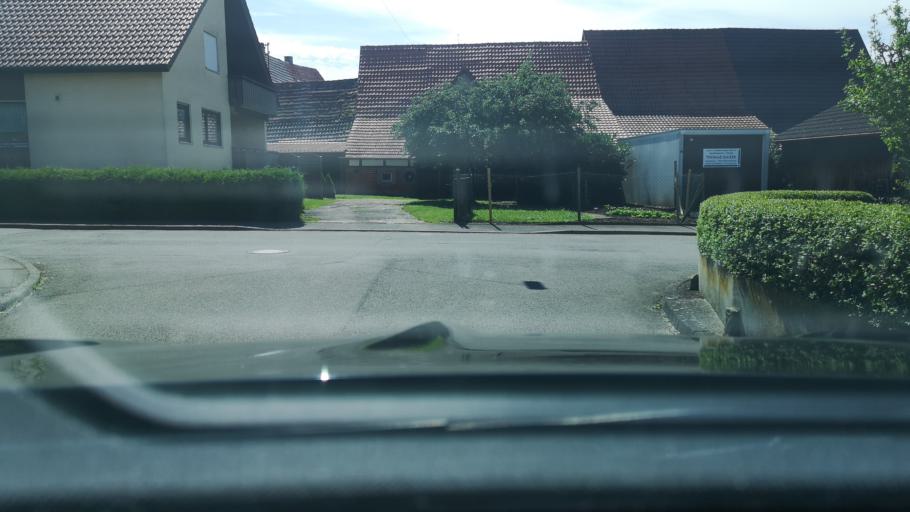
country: DE
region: Baden-Wuerttemberg
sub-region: Tuebingen Region
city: Pliezhausen
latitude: 48.5885
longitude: 9.1821
